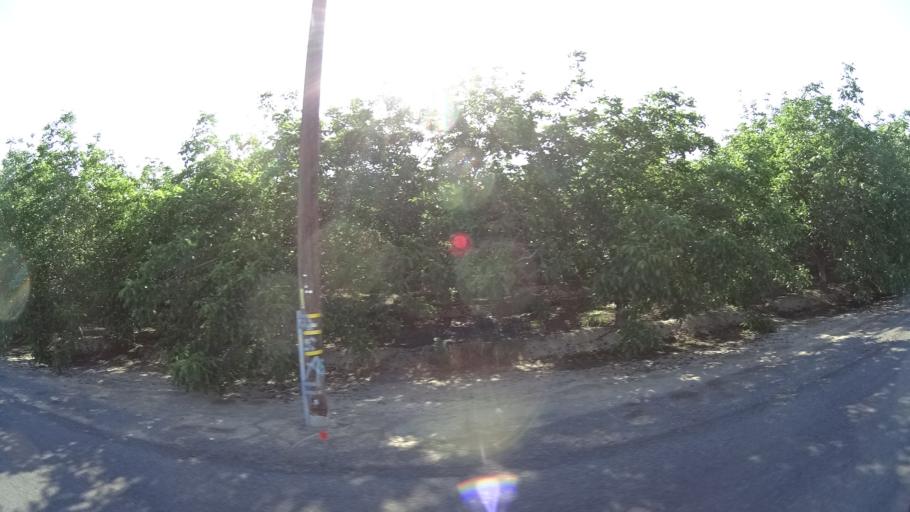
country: US
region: California
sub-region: Fresno County
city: Laton
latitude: 36.4131
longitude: -119.7133
